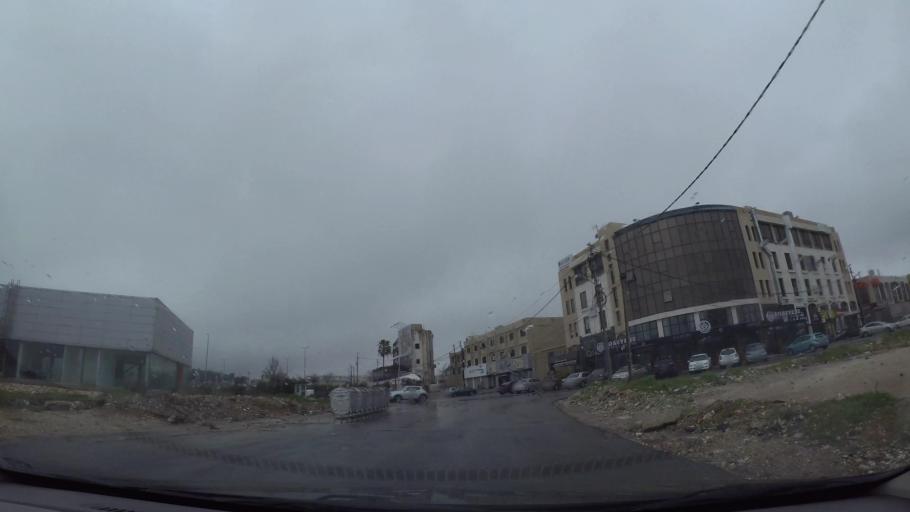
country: JO
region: Amman
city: Wadi as Sir
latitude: 31.9727
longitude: 35.8407
